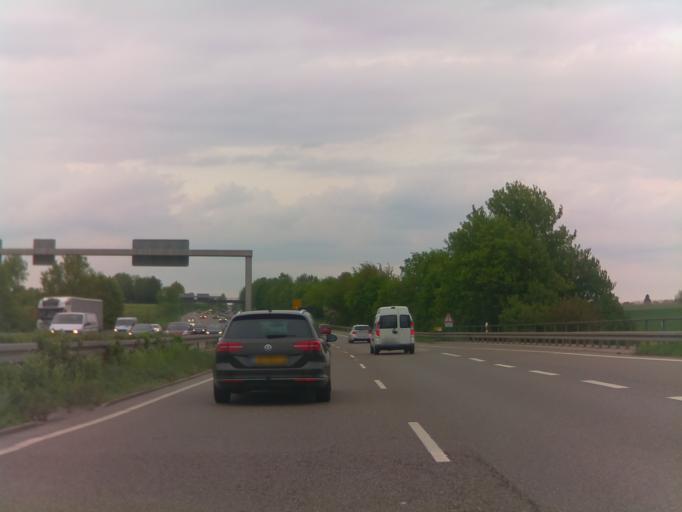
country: DE
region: Baden-Wuerttemberg
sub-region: Regierungsbezirk Stuttgart
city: Ehningen
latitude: 48.6900
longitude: 8.9688
